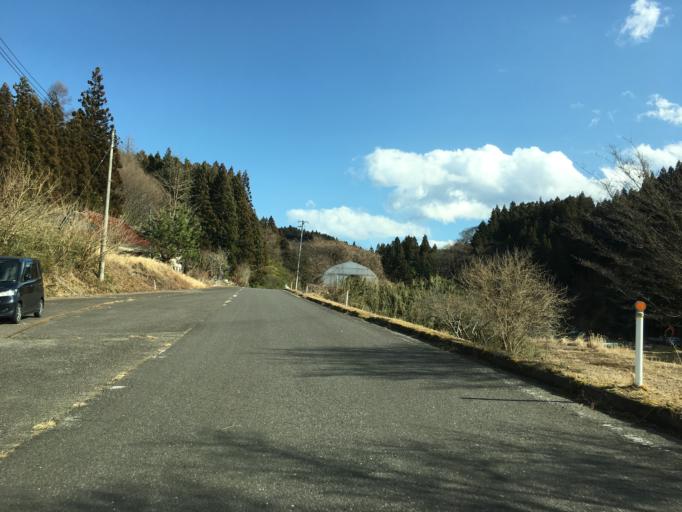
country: JP
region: Fukushima
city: Ishikawa
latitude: 37.2256
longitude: 140.5967
